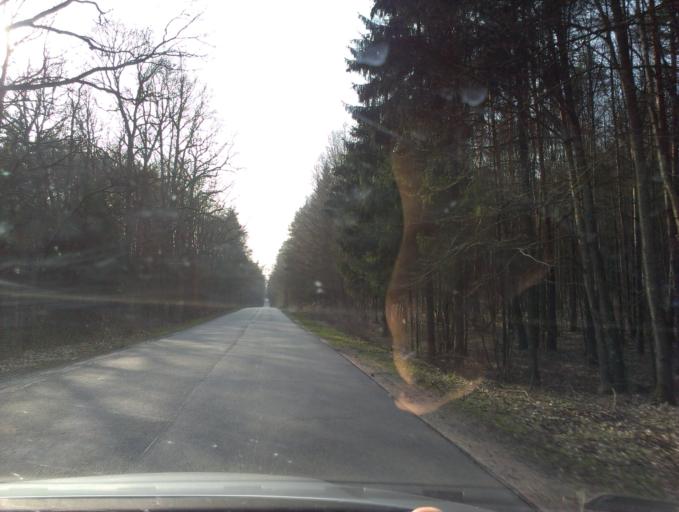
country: PL
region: Kujawsko-Pomorskie
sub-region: Powiat sepolenski
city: Sypniewo
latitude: 53.4507
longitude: 17.3826
